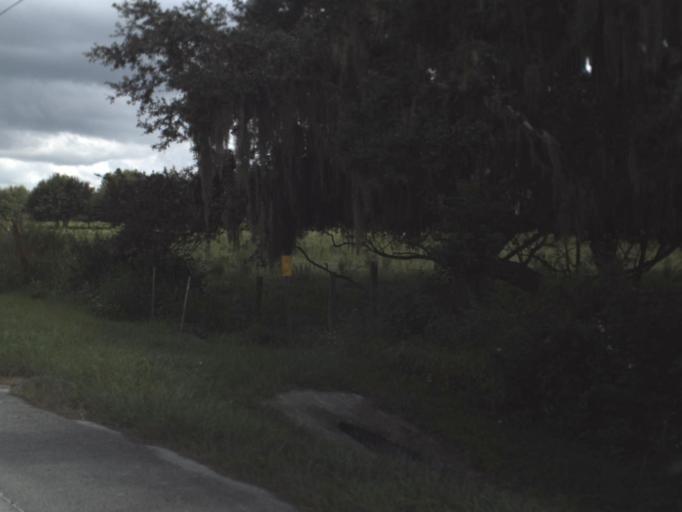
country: US
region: Florida
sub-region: Hardee County
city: Wauchula
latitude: 27.5508
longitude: -81.7009
